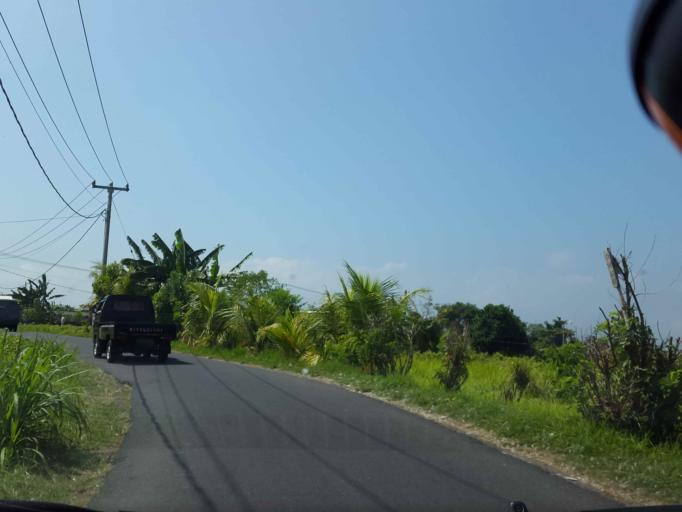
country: ID
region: Bali
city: Klungkung
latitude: -8.5542
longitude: 115.3682
